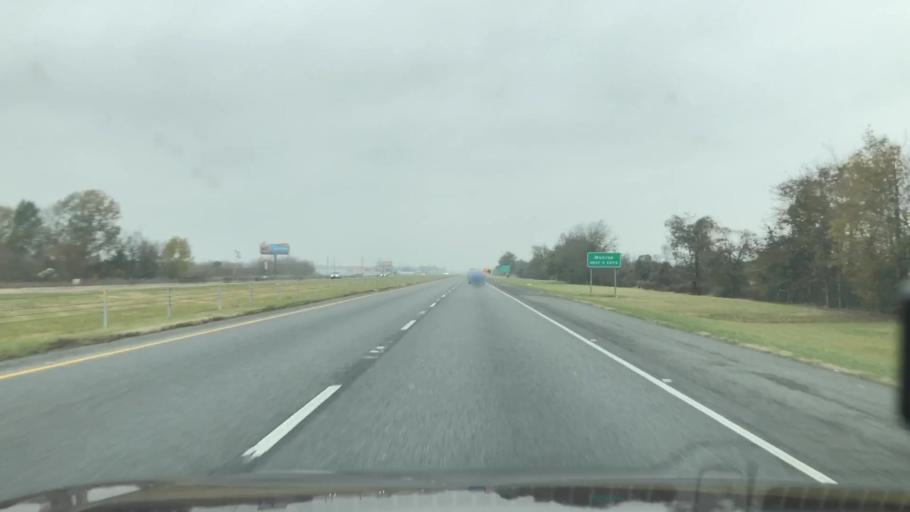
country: US
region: Louisiana
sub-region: Ouachita Parish
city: Lakeshore
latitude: 32.4910
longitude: -92.0123
